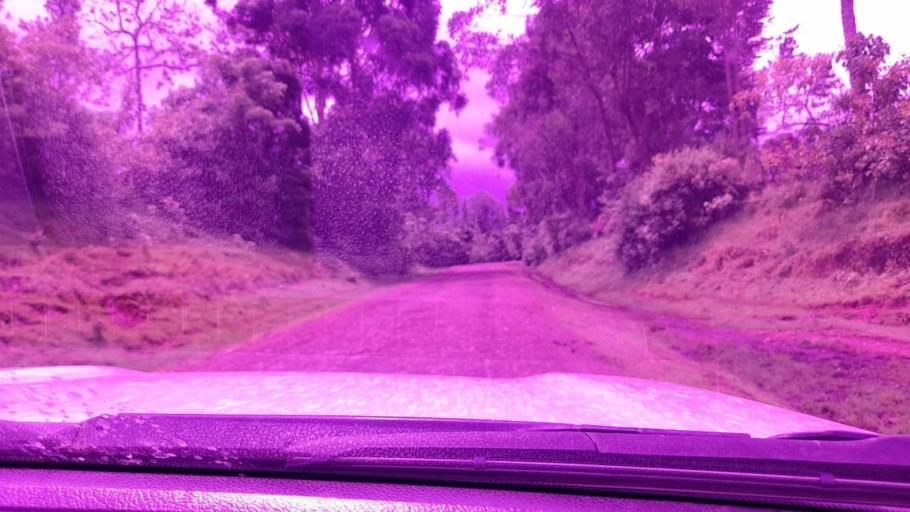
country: ET
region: Southern Nations, Nationalities, and People's Region
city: Tippi
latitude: 7.6169
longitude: 35.5840
